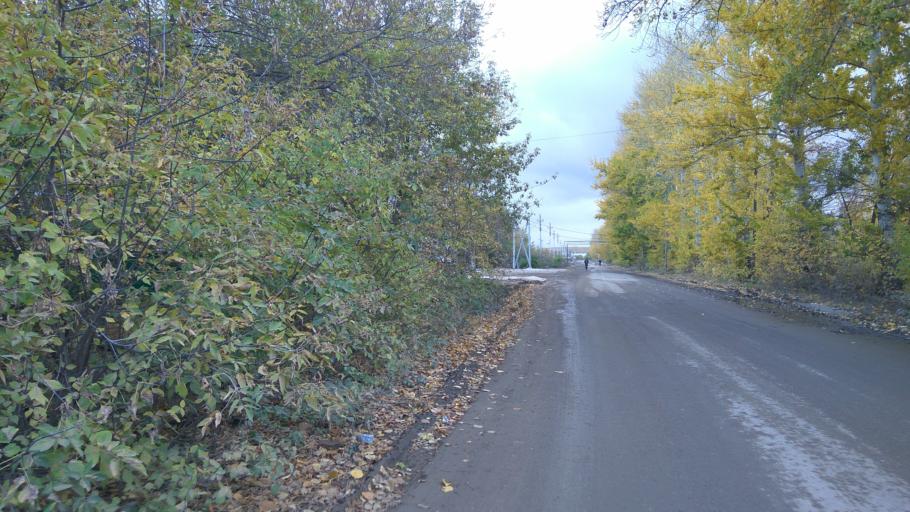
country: RU
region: Tatarstan
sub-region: Gorod Kazan'
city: Kazan
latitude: 55.7307
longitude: 49.1153
